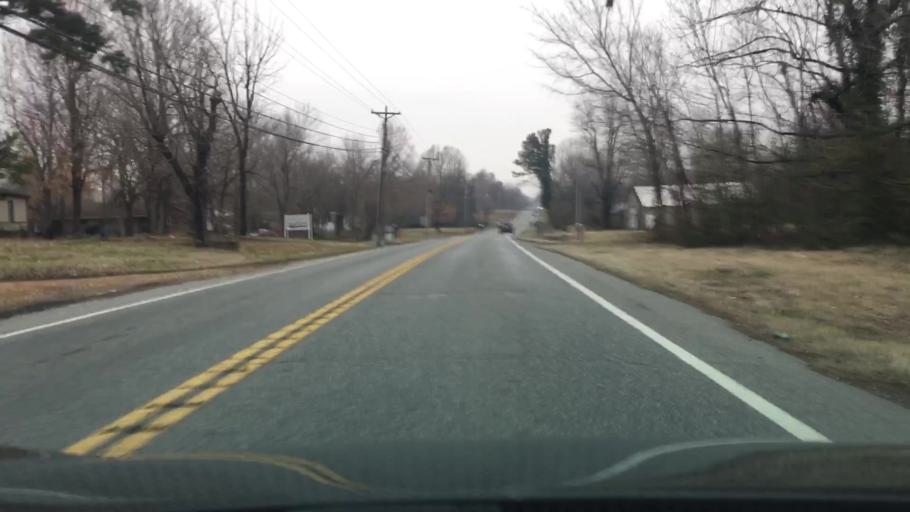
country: US
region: Kentucky
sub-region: Livingston County
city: Ledbetter
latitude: 36.9692
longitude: -88.4593
